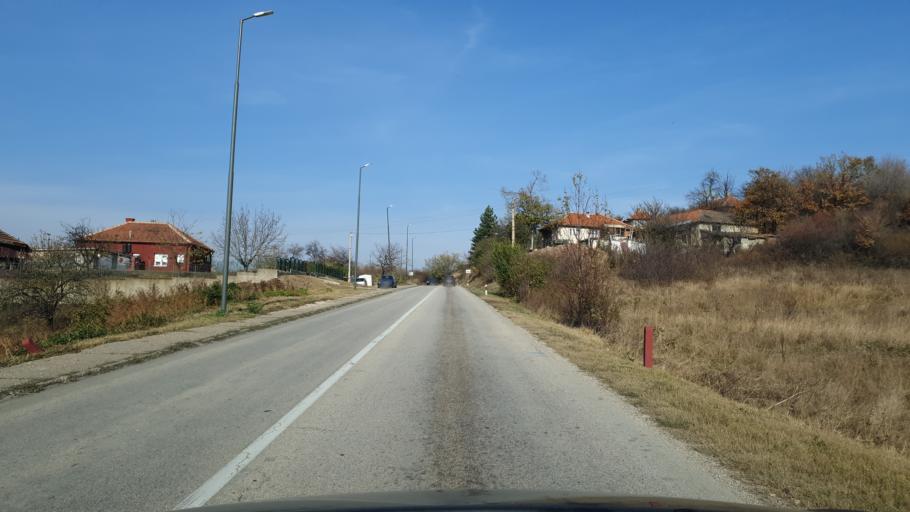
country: RS
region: Central Serbia
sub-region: Borski Okrug
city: Bor
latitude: 44.0516
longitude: 22.1039
